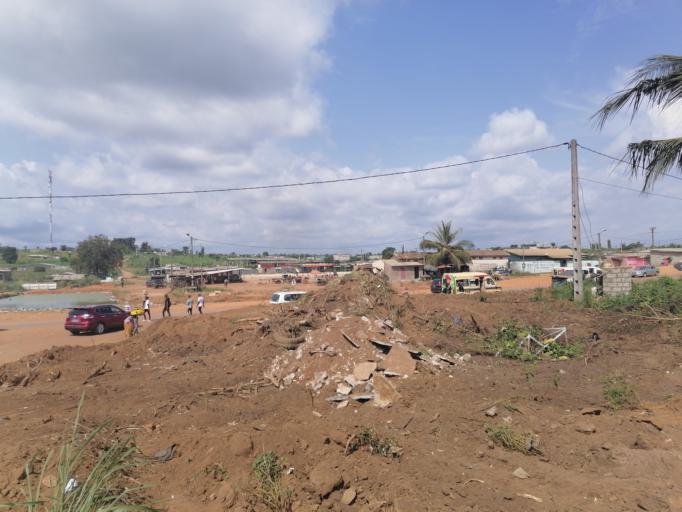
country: CI
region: Lagunes
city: Songon
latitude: 5.3207
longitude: -4.2315
